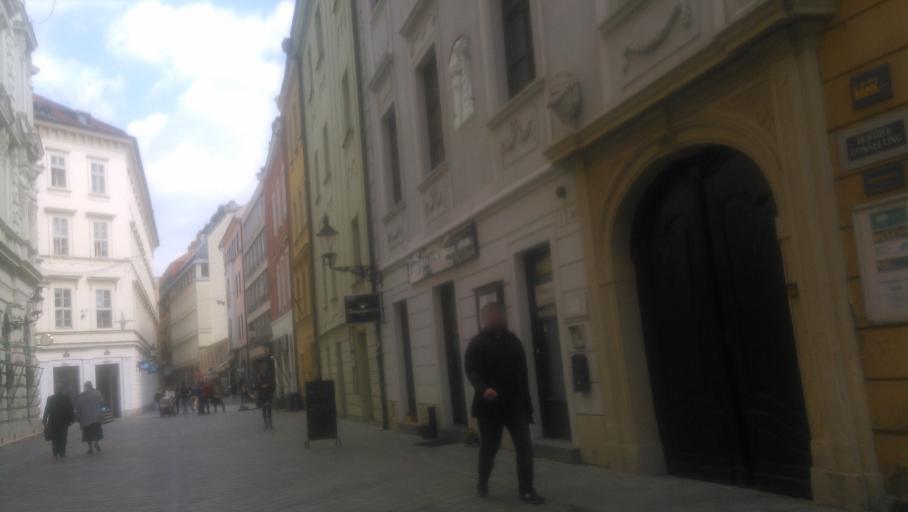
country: SK
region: Bratislavsky
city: Bratislava
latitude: 48.1428
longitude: 17.1083
